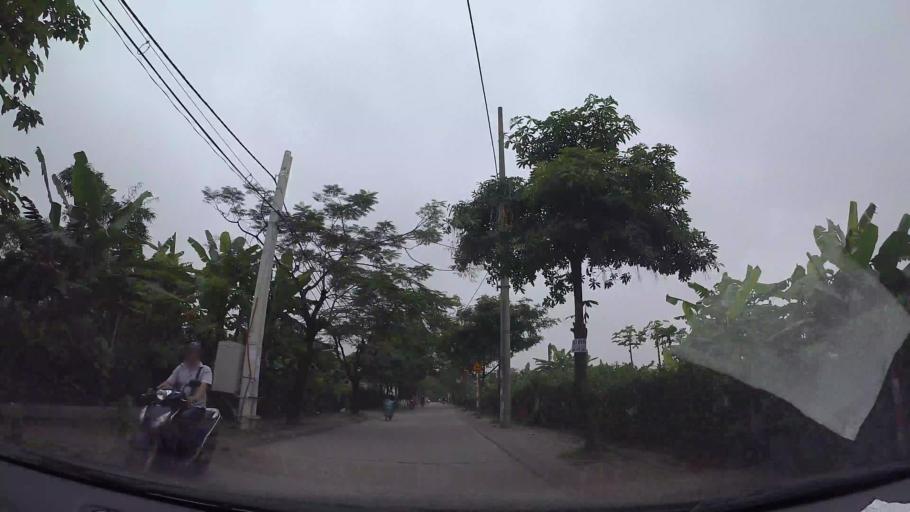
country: VN
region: Ha Noi
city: Hai BaTrung
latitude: 20.9956
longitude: 105.8830
